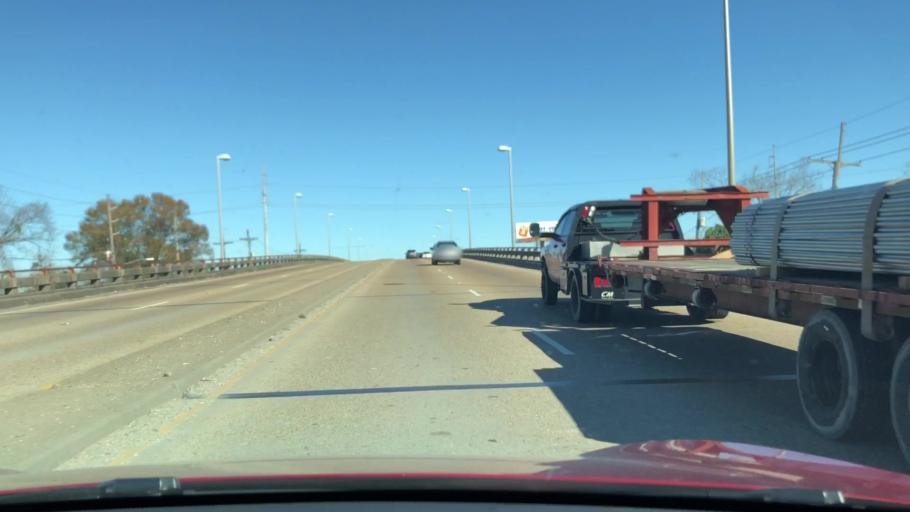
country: US
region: Louisiana
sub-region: Jefferson Parish
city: Jefferson
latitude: 29.9682
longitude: -90.1566
